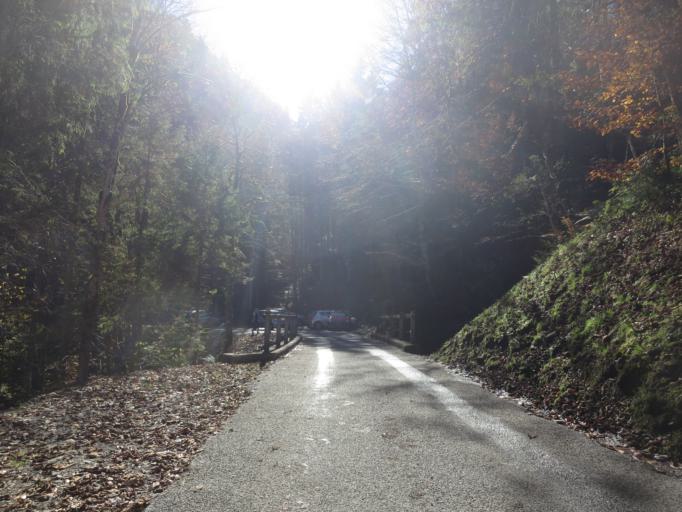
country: CH
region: Schwyz
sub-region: Bezirk March
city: Vorderthal
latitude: 47.0654
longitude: 8.9116
